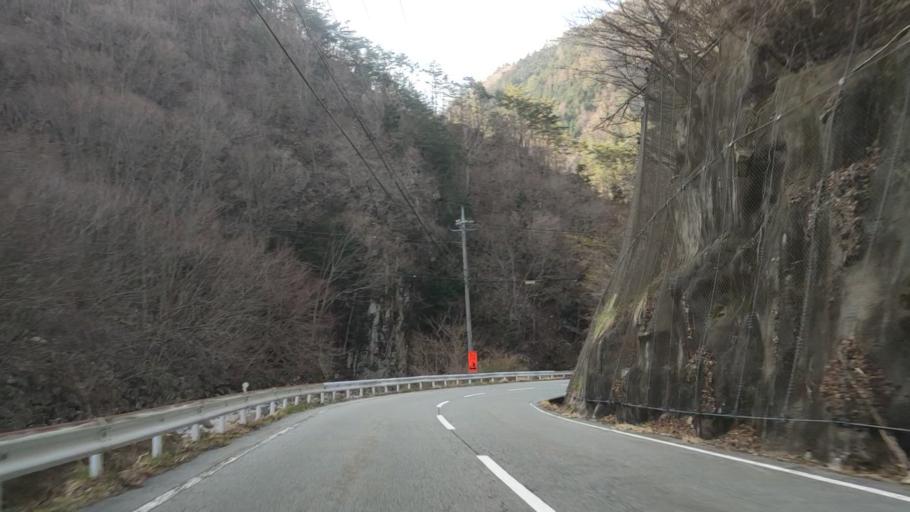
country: JP
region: Yamanashi
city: Fujikawaguchiko
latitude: 35.5419
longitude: 138.6406
